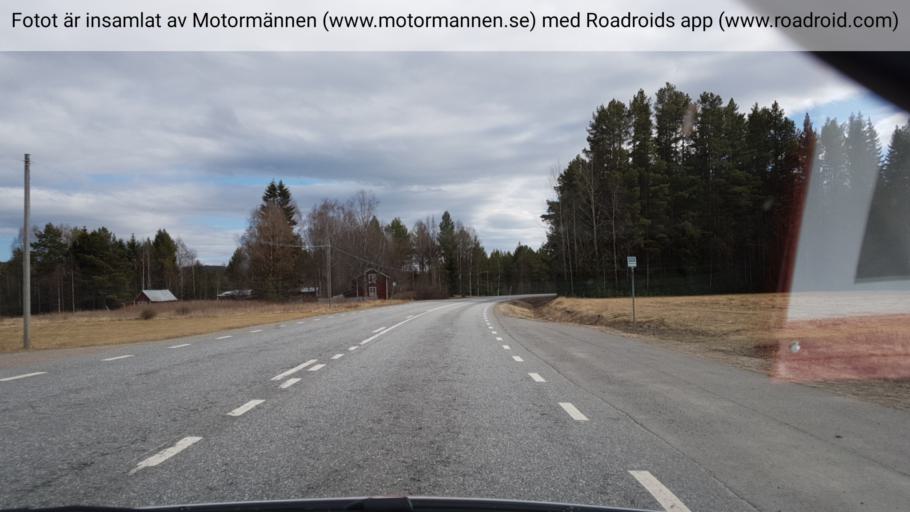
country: SE
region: Vaesternorrland
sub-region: Solleftea Kommun
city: Solleftea
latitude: 63.2594
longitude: 17.2183
